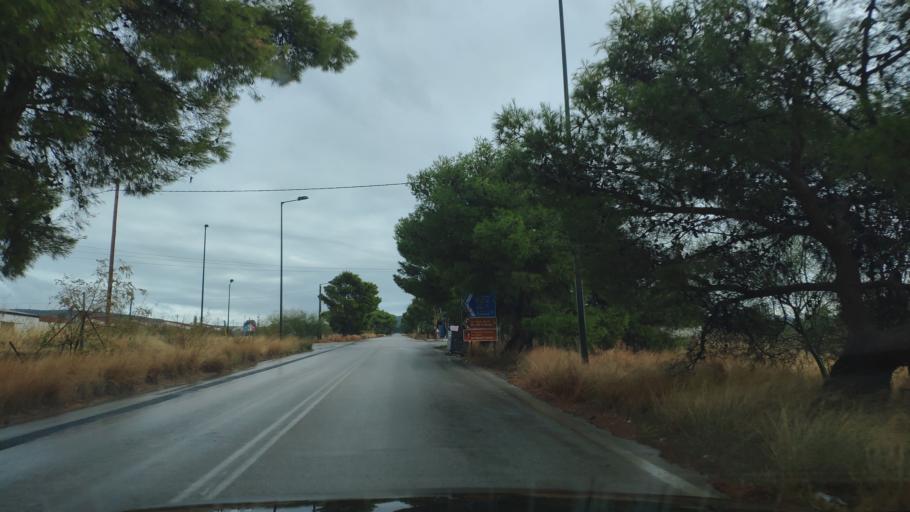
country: GR
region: Peloponnese
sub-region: Nomos Korinthias
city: Loutraki
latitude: 37.9663
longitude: 22.9862
